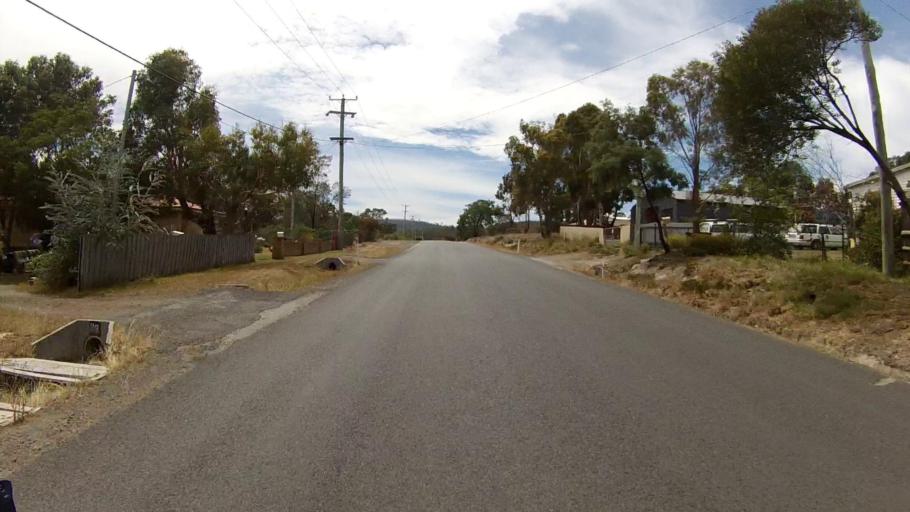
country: AU
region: Tasmania
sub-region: Sorell
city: Sorell
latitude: -42.8067
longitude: 147.6366
